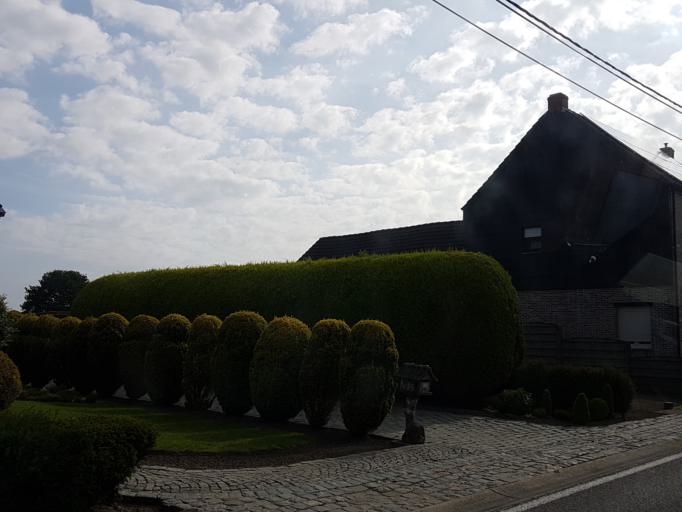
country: BE
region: Flanders
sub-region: Provincie Antwerpen
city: Westerlo
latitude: 51.1042
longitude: 4.8828
